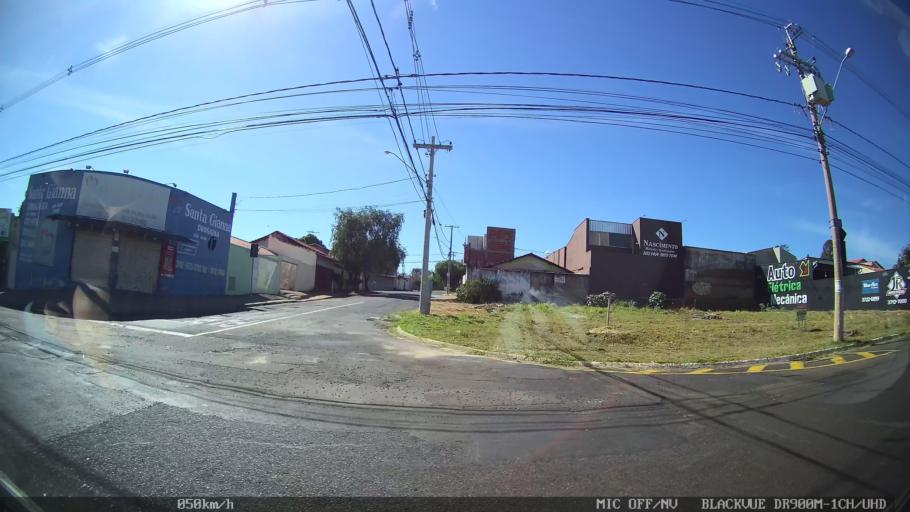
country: BR
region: Sao Paulo
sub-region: Franca
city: Franca
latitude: -20.5519
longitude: -47.3719
